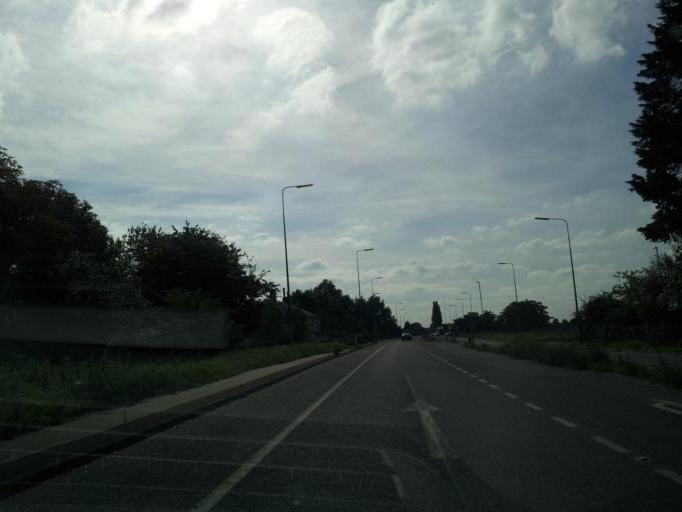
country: GB
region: England
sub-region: Cambridgeshire
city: Waterbeach
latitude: 52.2643
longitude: 0.1796
